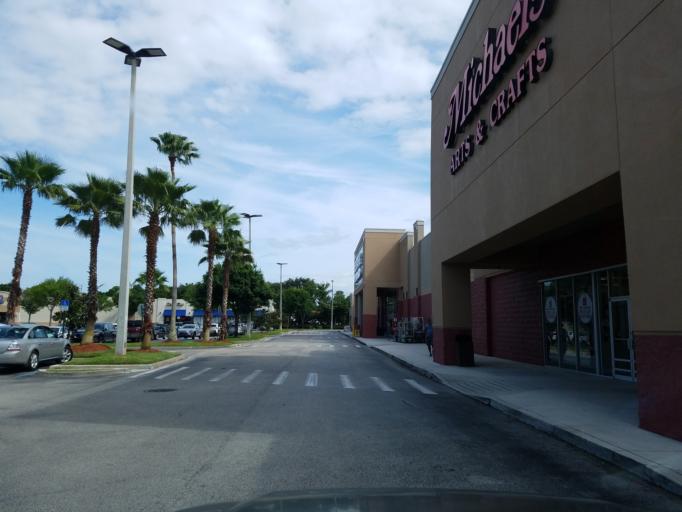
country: US
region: Florida
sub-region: Martin County
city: North River Shores
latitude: 27.2357
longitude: -80.2701
